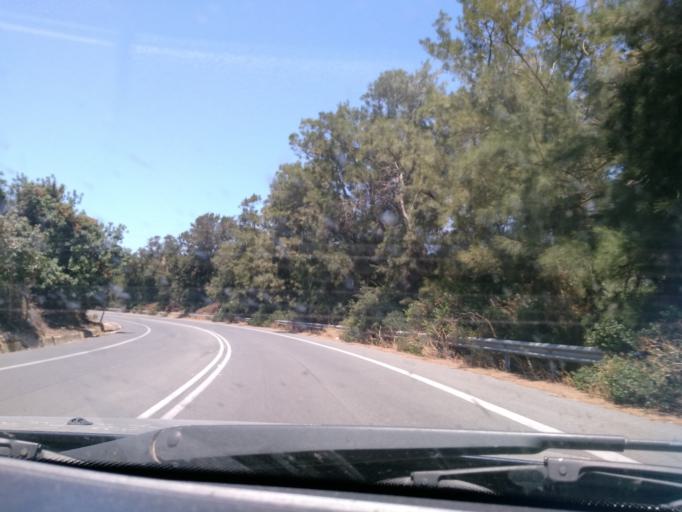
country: GR
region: Crete
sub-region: Nomos Rethymnis
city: Anogeia
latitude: 35.3977
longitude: 24.8784
